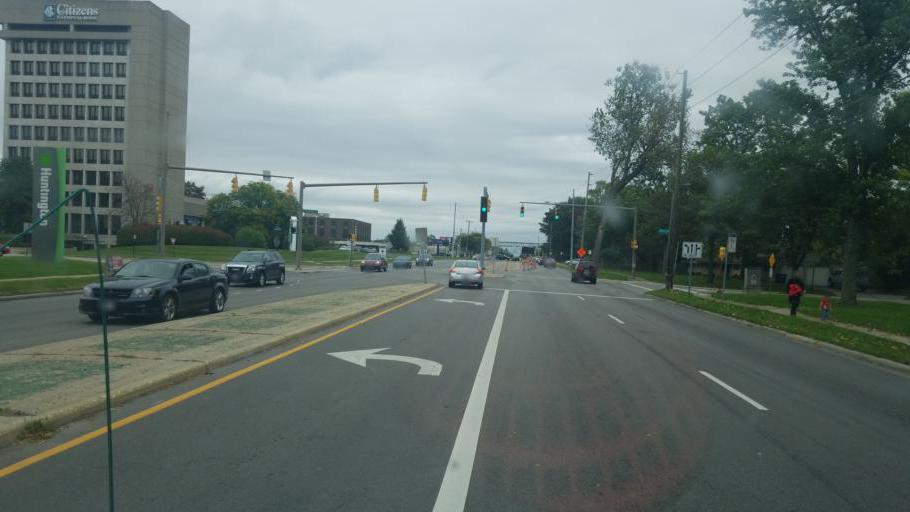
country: US
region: Ohio
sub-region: Lucas County
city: Ottawa Hills
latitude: 41.6772
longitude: -83.6301
